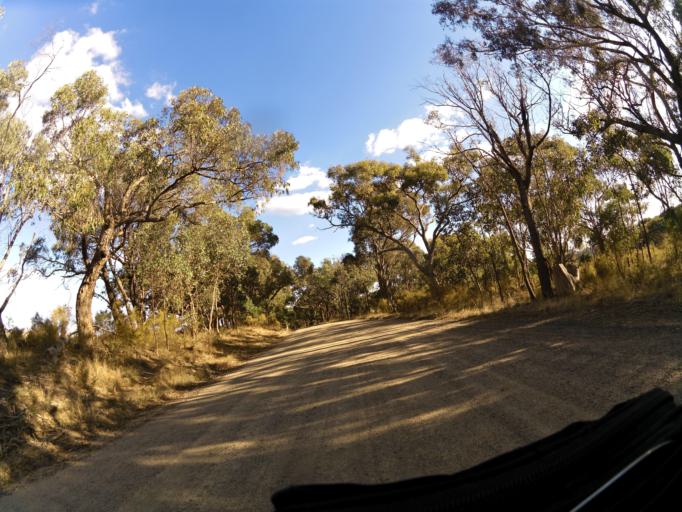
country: AU
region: Victoria
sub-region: Greater Bendigo
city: Kennington
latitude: -37.0218
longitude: 144.8008
